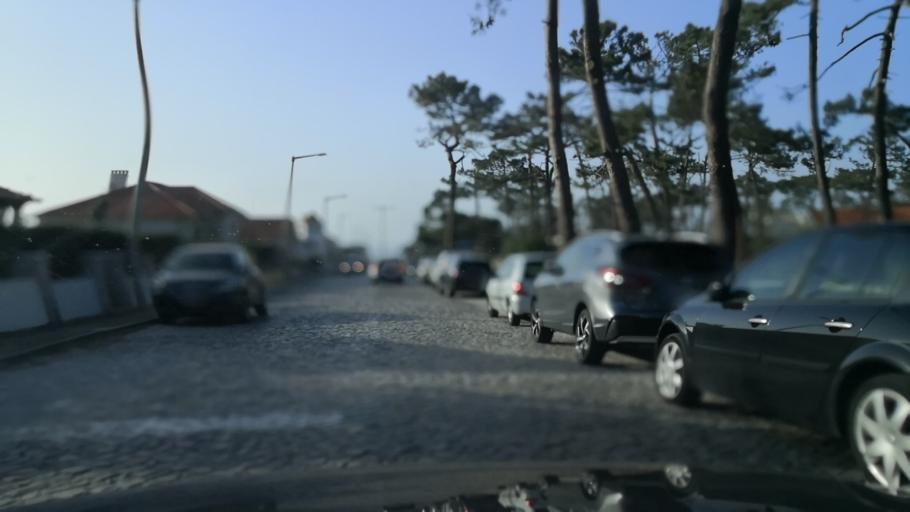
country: PT
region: Leiria
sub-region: Alcobaca
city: Pataias
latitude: 39.7572
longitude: -9.0283
